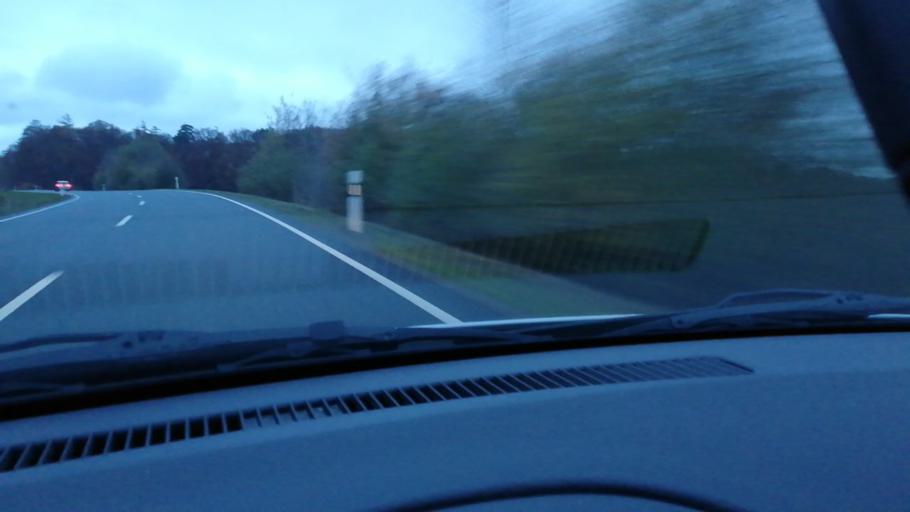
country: DE
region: Bavaria
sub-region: Regierungsbezirk Unterfranken
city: Bischbrunn
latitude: 49.8798
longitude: 9.4912
